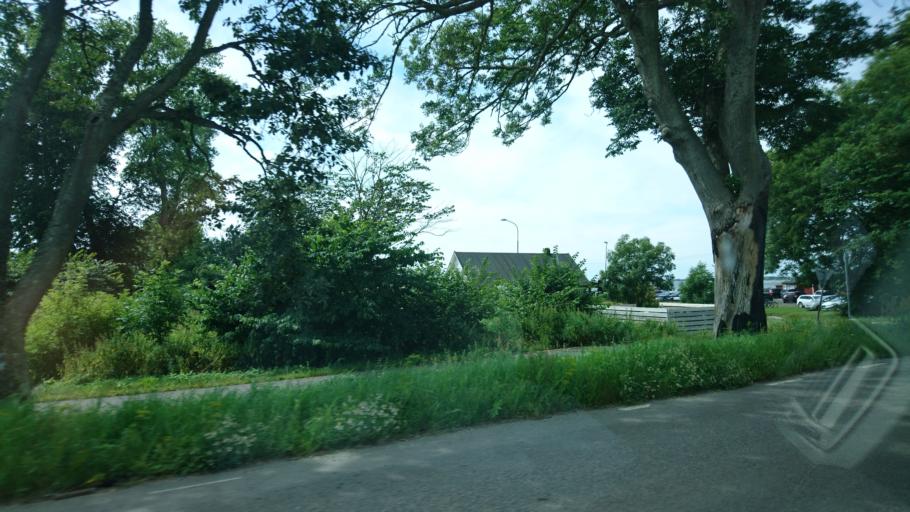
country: SE
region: Skane
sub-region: Skurups Kommun
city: Skivarp
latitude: 55.3866
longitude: 13.5492
